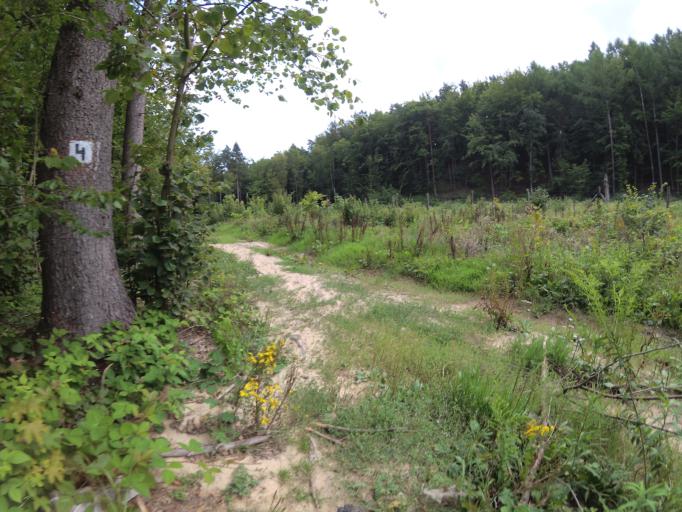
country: PL
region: Pomeranian Voivodeship
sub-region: Gdynia
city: Wielki Kack
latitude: 54.4890
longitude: 18.4472
